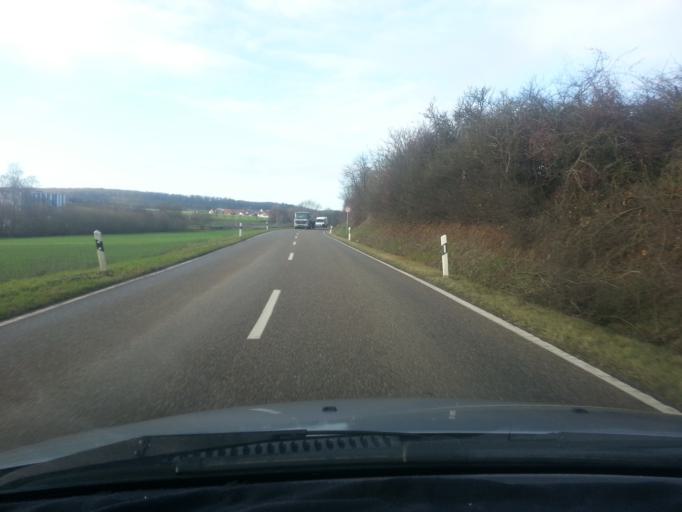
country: DE
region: Baden-Wuerttemberg
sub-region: Karlsruhe Region
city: Sulzfeld
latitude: 49.1695
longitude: 8.8481
